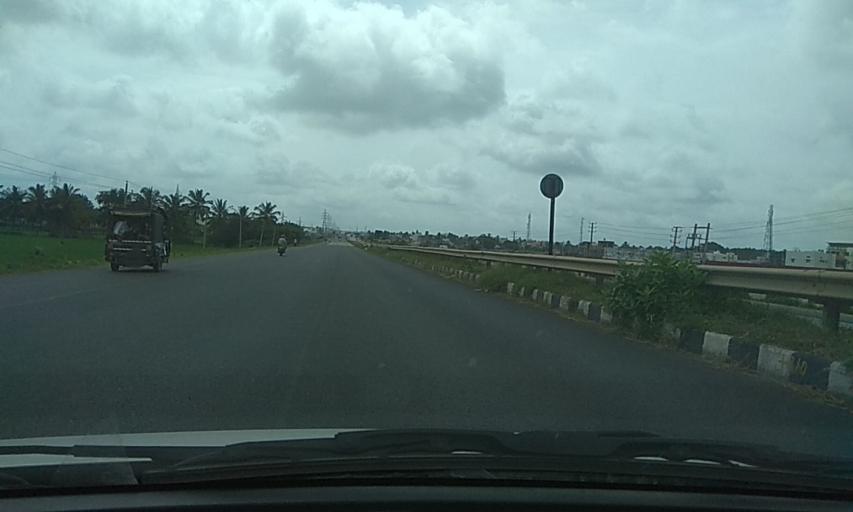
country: IN
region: Karnataka
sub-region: Davanagere
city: Harihar
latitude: 14.4450
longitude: 75.8907
